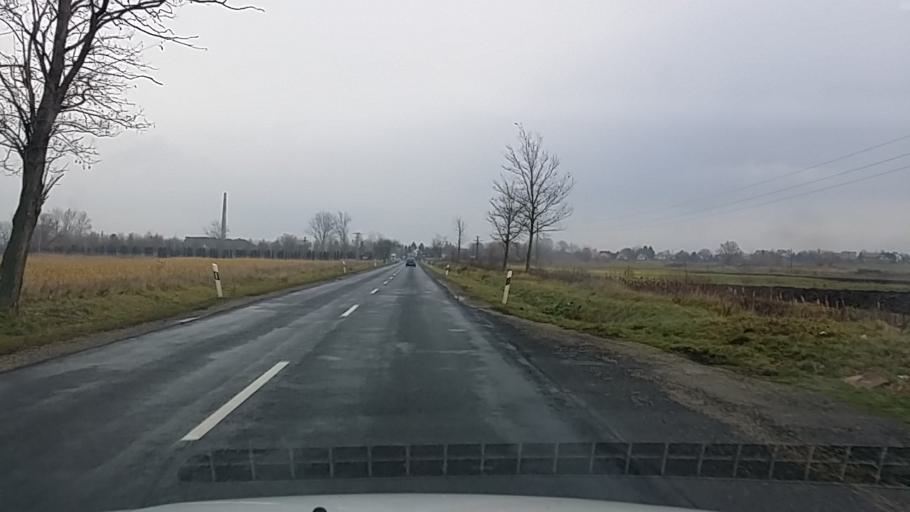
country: HU
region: Veszprem
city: Papa
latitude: 47.3095
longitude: 17.4180
